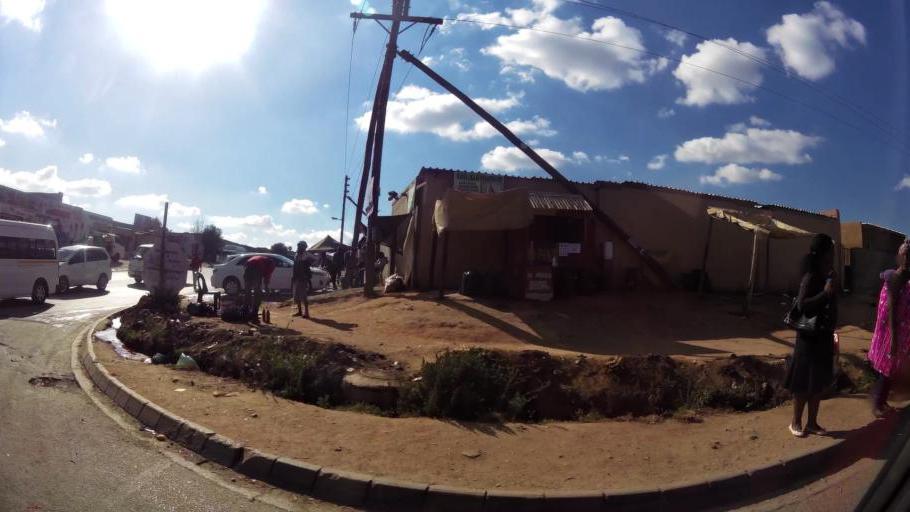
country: ZA
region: Gauteng
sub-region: West Rand District Municipality
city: Muldersdriseloop
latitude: -26.0313
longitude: 27.9254
